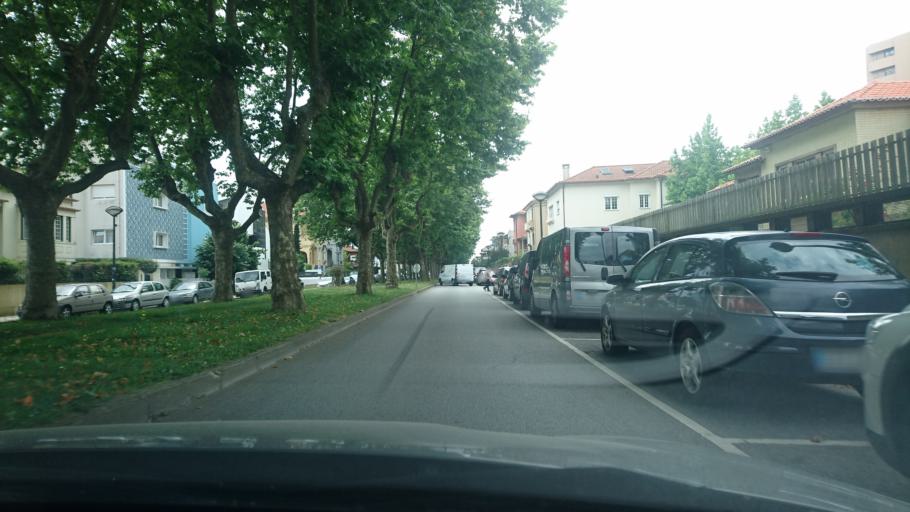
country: PT
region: Porto
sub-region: Porto
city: Porto
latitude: 41.1649
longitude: -8.5937
